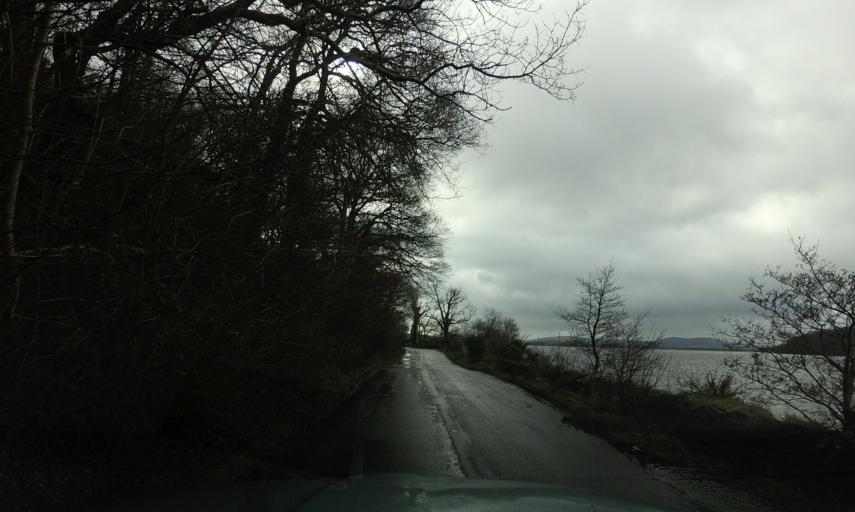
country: GB
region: Scotland
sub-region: West Dunbartonshire
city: Balloch
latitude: 56.1154
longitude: -4.5857
